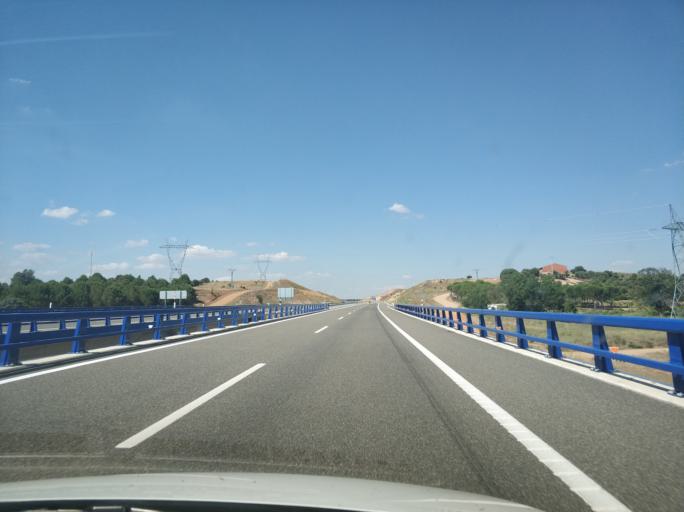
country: ES
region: Castille and Leon
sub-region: Provincia de Zamora
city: Granja de Moreruela
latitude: 41.8102
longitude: -5.7501
